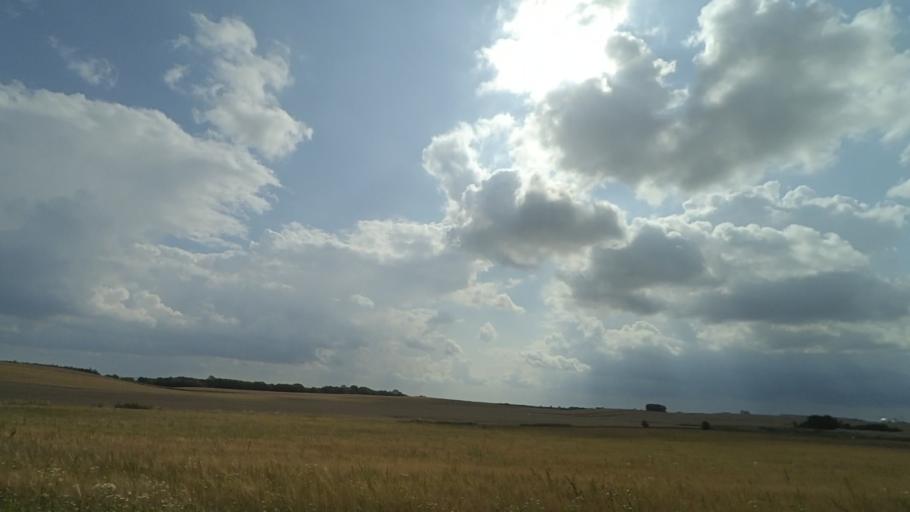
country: DK
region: Central Jutland
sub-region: Norddjurs Kommune
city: Allingabro
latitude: 56.5359
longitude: 10.3631
